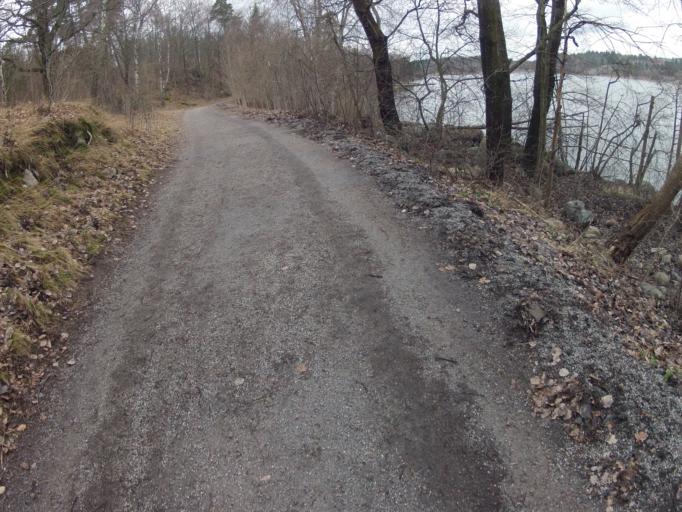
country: SE
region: Stockholm
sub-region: Norrtalje Kommun
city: Bergshamra
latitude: 59.3715
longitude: 18.0271
